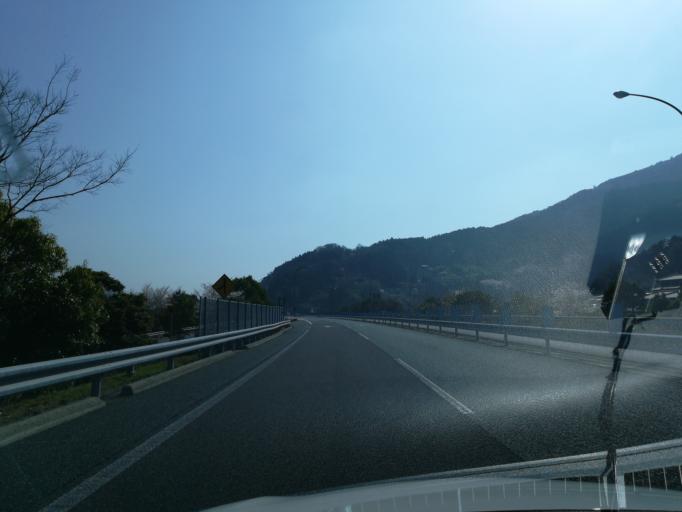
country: JP
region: Tokushima
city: Ikedacho
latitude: 34.0287
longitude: 133.8390
